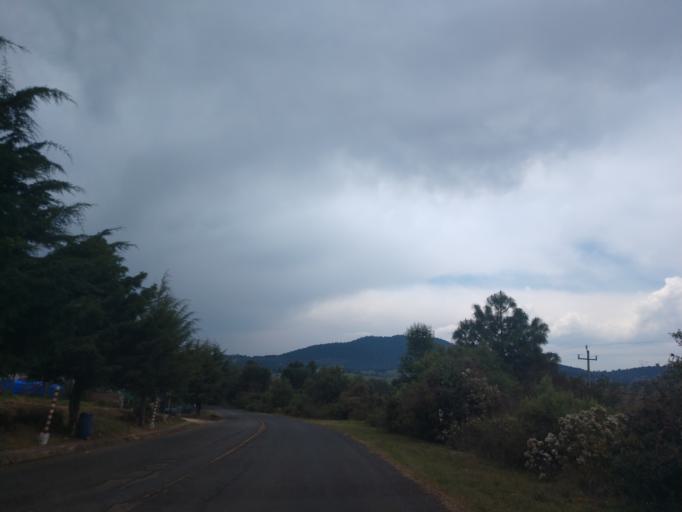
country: MX
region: Jalisco
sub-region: Mazamitla
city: Mazamitla
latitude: 19.9234
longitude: -103.0413
